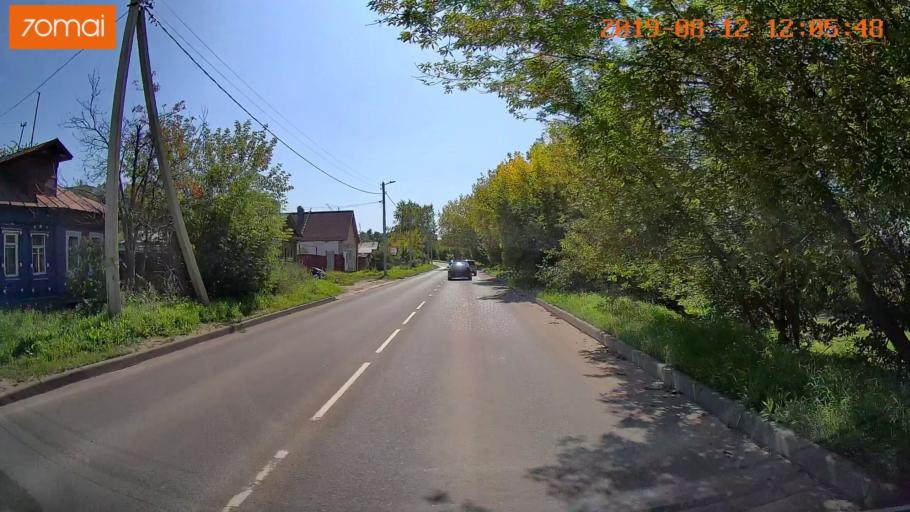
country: RU
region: Ivanovo
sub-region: Gorod Ivanovo
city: Ivanovo
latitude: 56.9923
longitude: 41.0188
